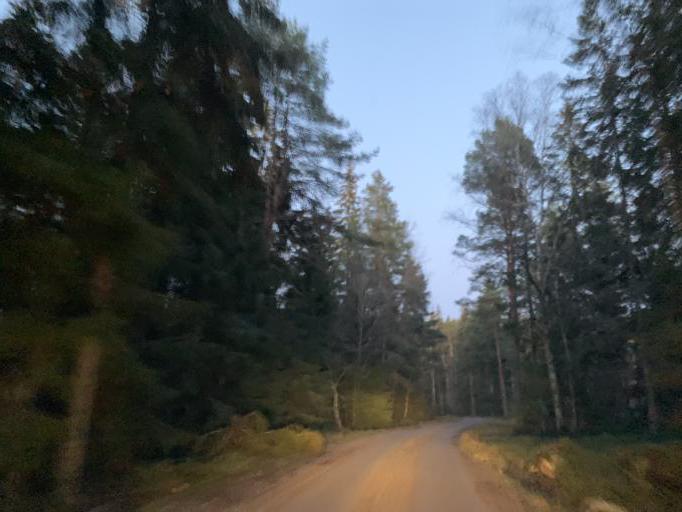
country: SE
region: OErebro
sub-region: Lindesbergs Kommun
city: Fellingsbro
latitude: 59.3531
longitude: 15.5725
